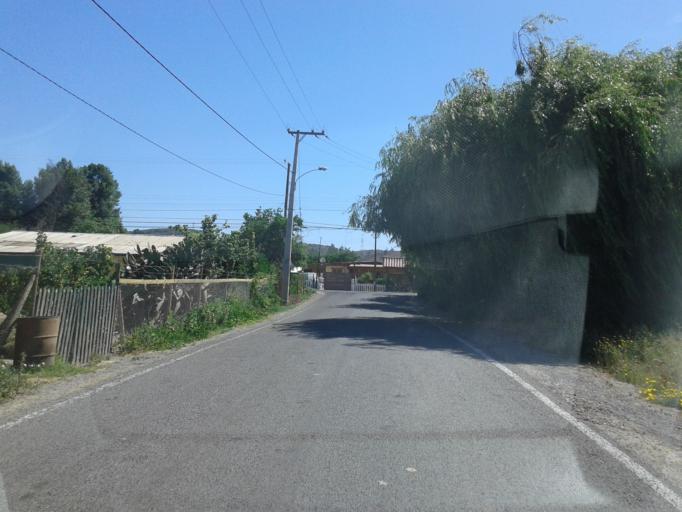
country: CL
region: Valparaiso
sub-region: Provincia de Marga Marga
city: Limache
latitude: -32.9754
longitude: -71.2938
